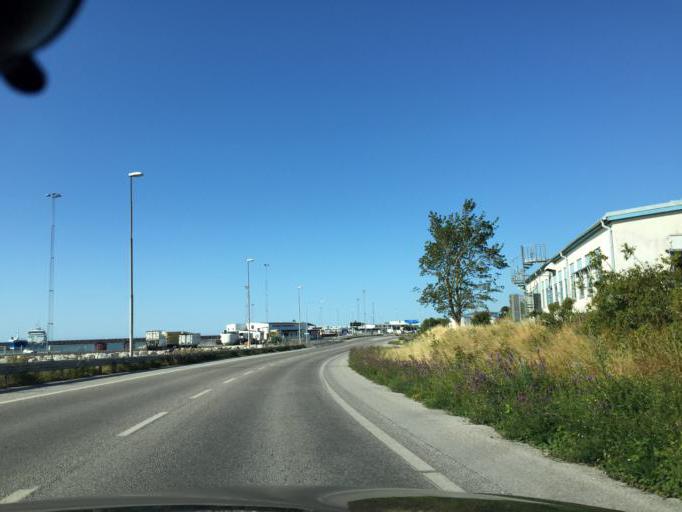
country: SE
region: Gotland
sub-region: Gotland
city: Visby
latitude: 57.6285
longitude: 18.2749
